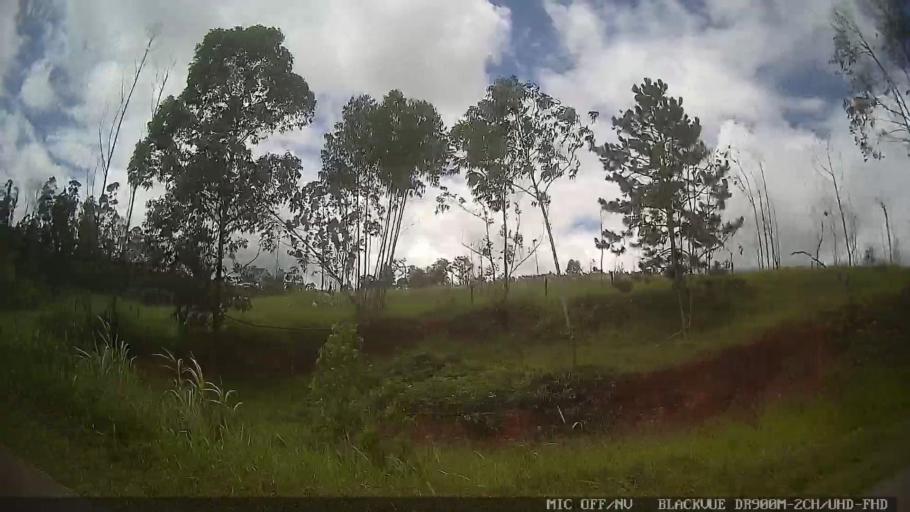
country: BR
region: Sao Paulo
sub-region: Braganca Paulista
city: Braganca Paulista
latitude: -22.8019
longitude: -46.5187
